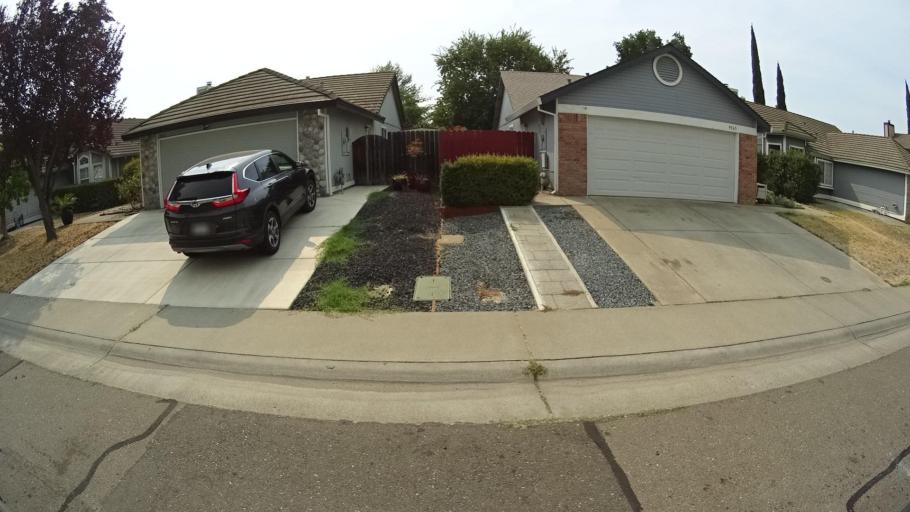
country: US
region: California
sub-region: Sacramento County
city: Laguna
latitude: 38.4114
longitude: -121.4014
